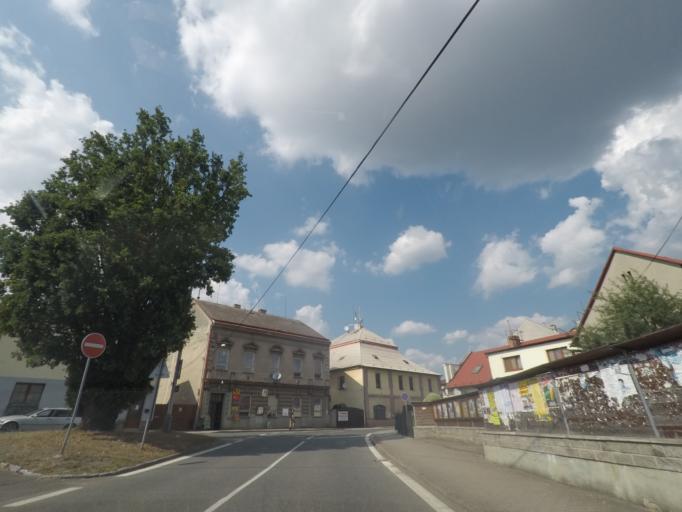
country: CZ
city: Borohradek
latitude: 50.0966
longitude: 16.0917
